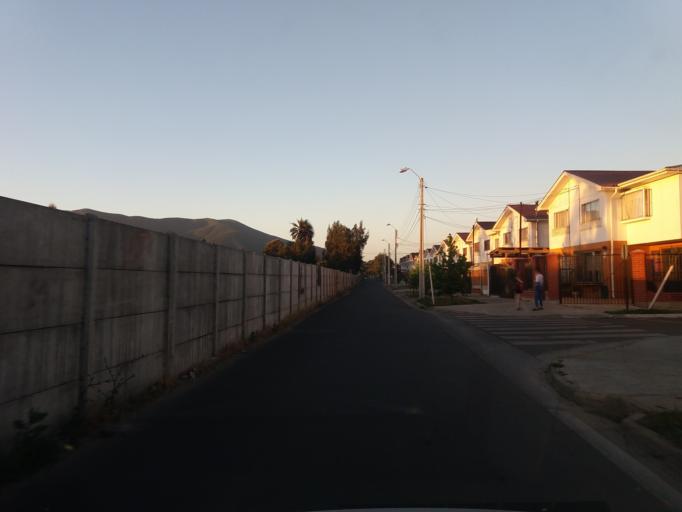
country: CL
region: Valparaiso
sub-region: Provincia de Quillota
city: Quillota
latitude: -32.8867
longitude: -71.2556
